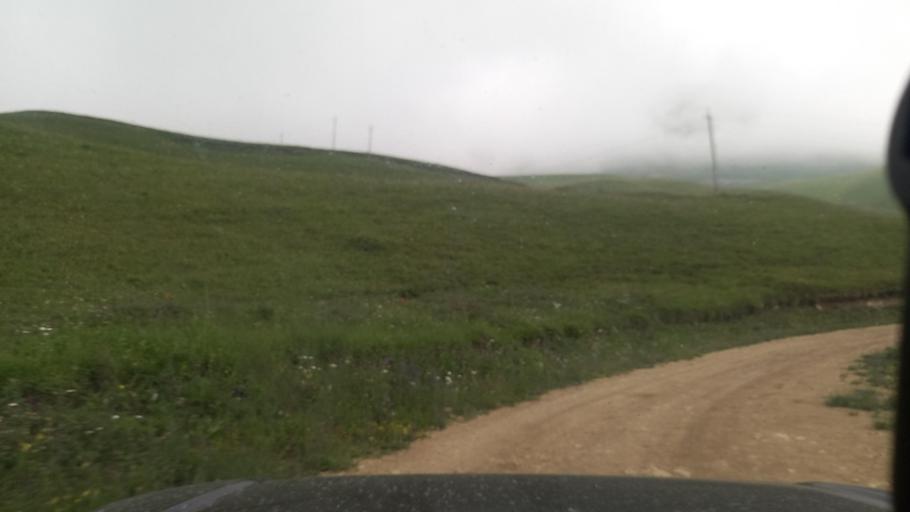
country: RU
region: Karachayevo-Cherkesiya
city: Pregradnaya
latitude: 44.0092
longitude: 41.1670
